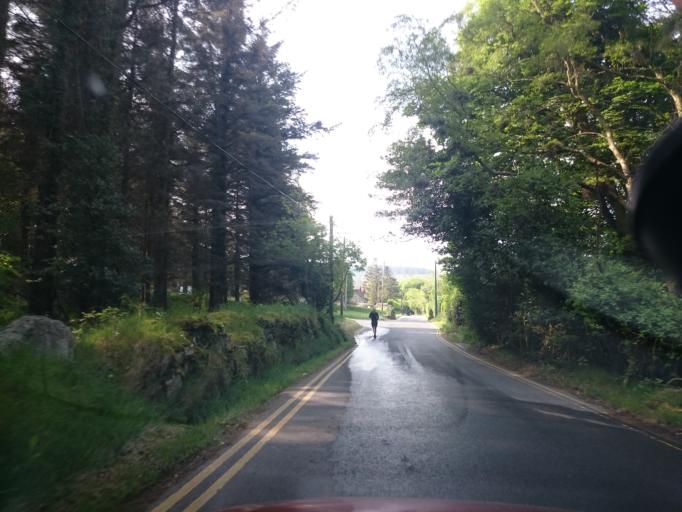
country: IE
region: Leinster
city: Ballinteer
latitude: 53.2561
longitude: -6.2508
